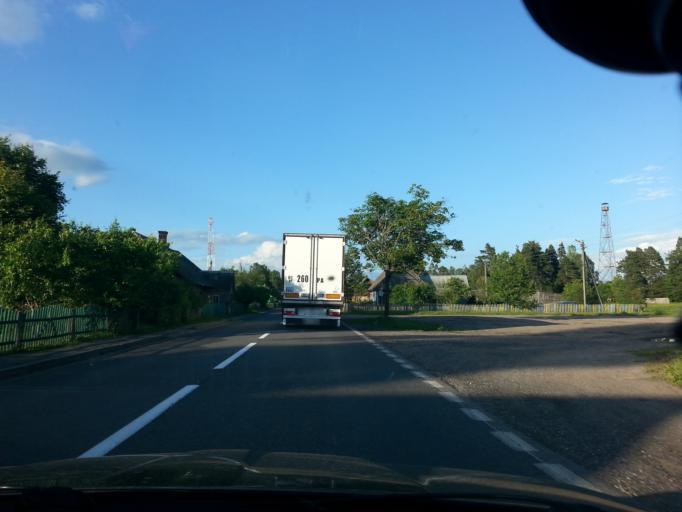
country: BY
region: Minsk
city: Svir
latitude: 54.9190
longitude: 26.4590
